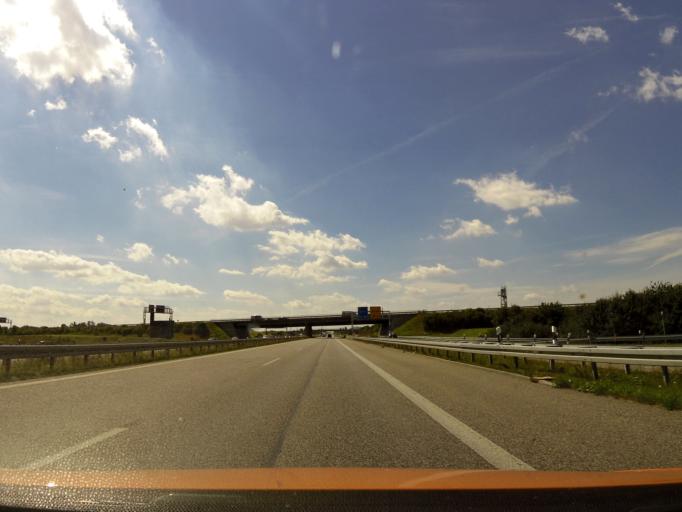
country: DE
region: Brandenburg
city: Gramzow
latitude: 53.2471
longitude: 14.0139
